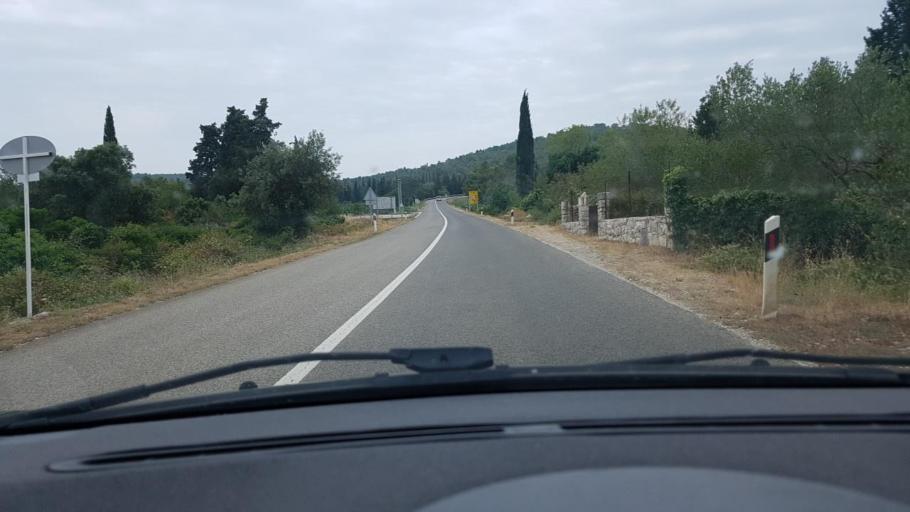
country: HR
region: Dubrovacko-Neretvanska
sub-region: Grad Korcula
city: Zrnovo
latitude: 42.9386
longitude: 17.1042
